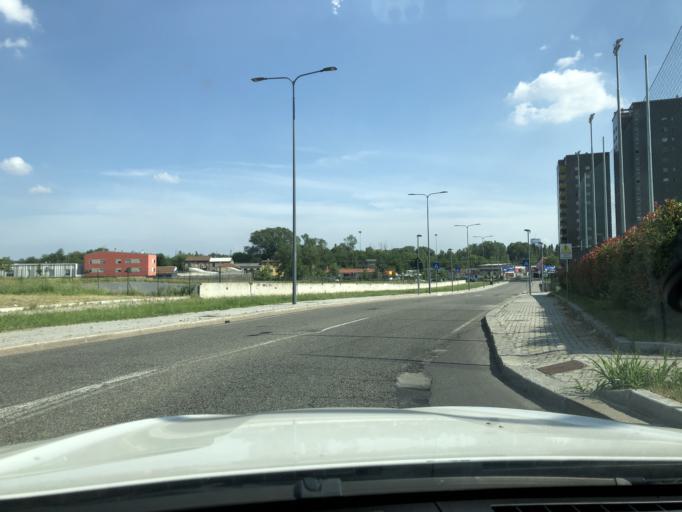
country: IT
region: Lombardy
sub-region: Citta metropolitana di Milano
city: Novate Milanese
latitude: 45.5113
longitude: 9.1471
